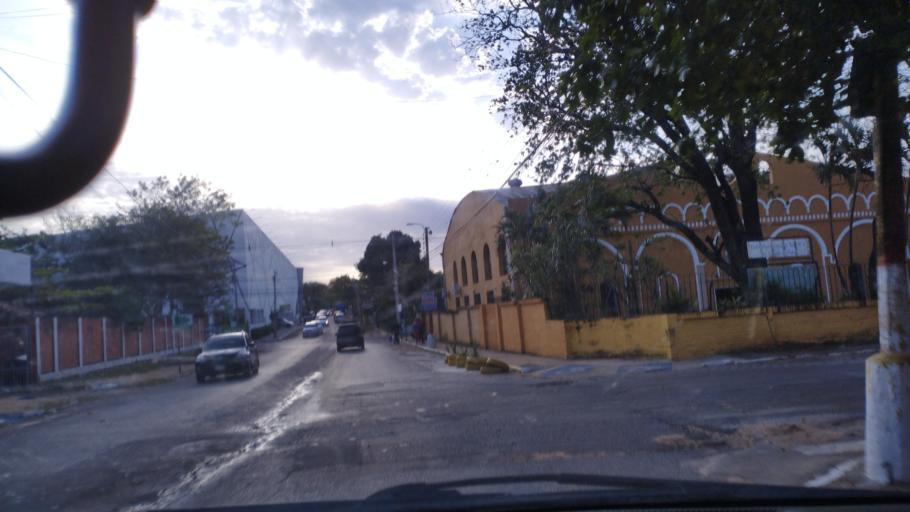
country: PY
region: Central
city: Fernando de la Mora
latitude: -25.3125
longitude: -57.5412
